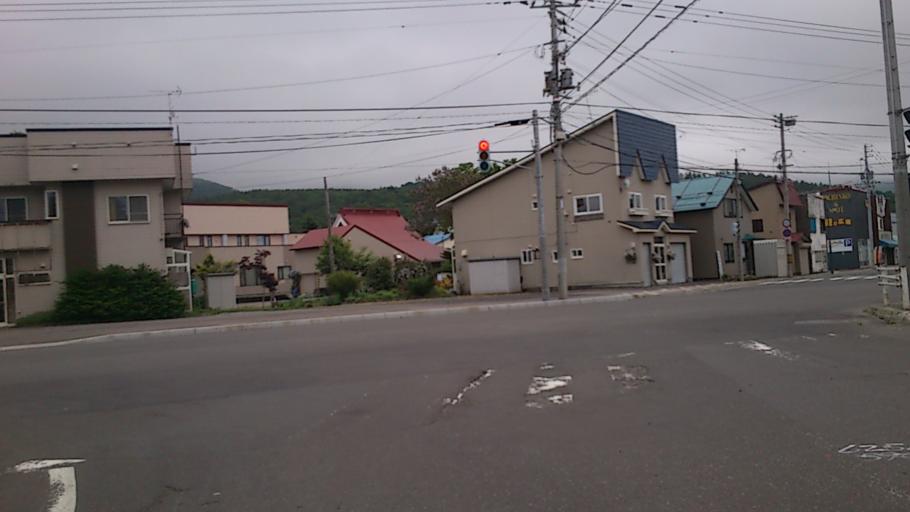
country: JP
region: Hokkaido
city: Niseko Town
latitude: 42.8081
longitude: 140.5296
